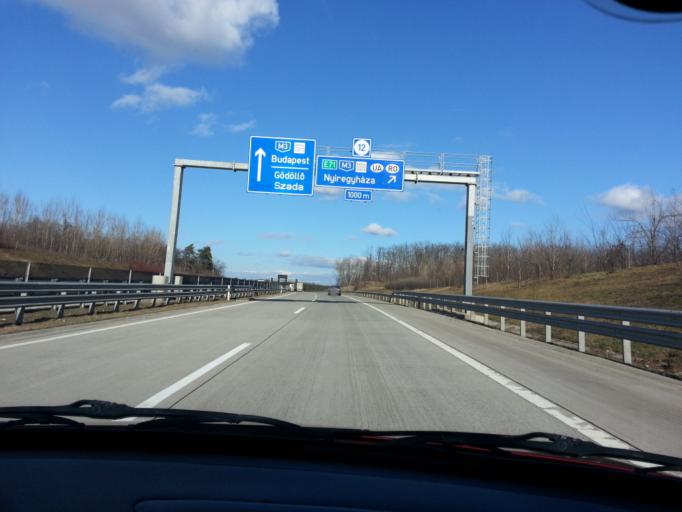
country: HU
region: Pest
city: Godollo
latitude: 47.5968
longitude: 19.3198
